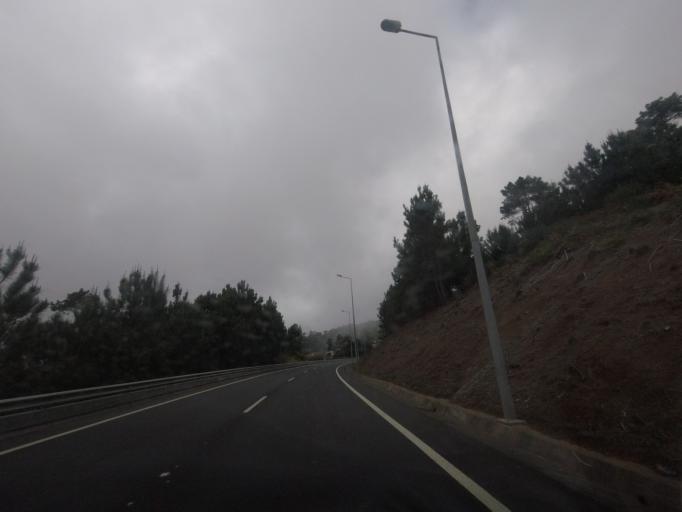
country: PT
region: Madeira
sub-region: Calheta
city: Estreito da Calheta
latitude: 32.7609
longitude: -17.2051
